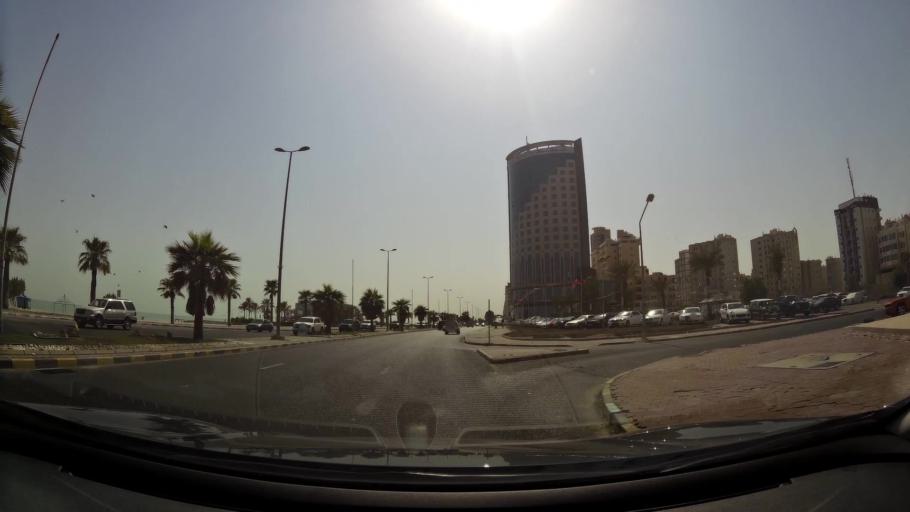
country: KW
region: Muhafazat Hawalli
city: As Salimiyah
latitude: 29.3421
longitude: 48.0967
